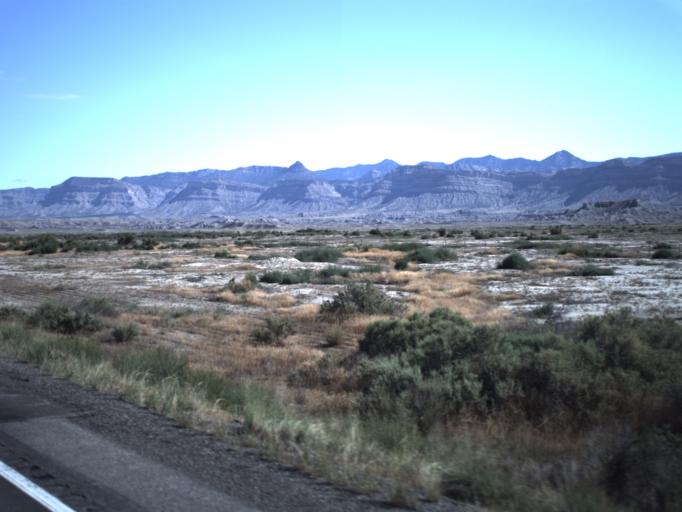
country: US
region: Utah
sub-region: Carbon County
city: East Carbon City
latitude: 39.3258
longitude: -110.3668
